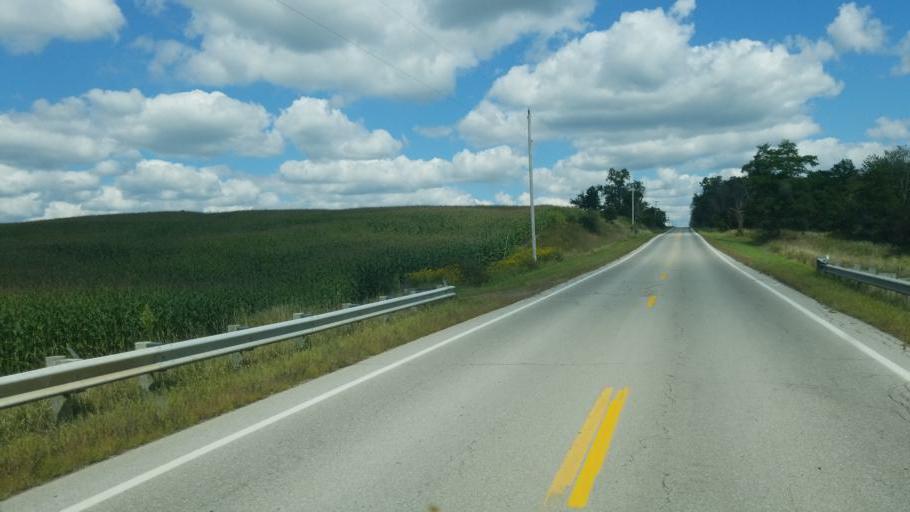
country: US
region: Ohio
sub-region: Wayne County
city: West Salem
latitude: 40.9795
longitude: -82.2363
